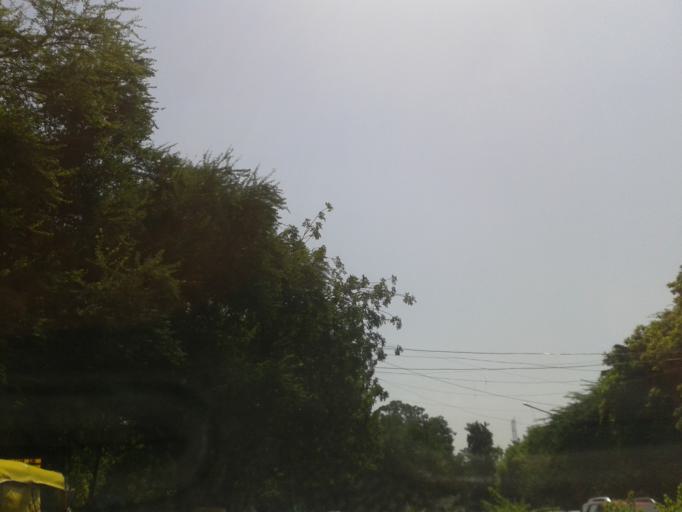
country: IN
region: NCT
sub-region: New Delhi
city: New Delhi
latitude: 28.6278
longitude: 77.2053
